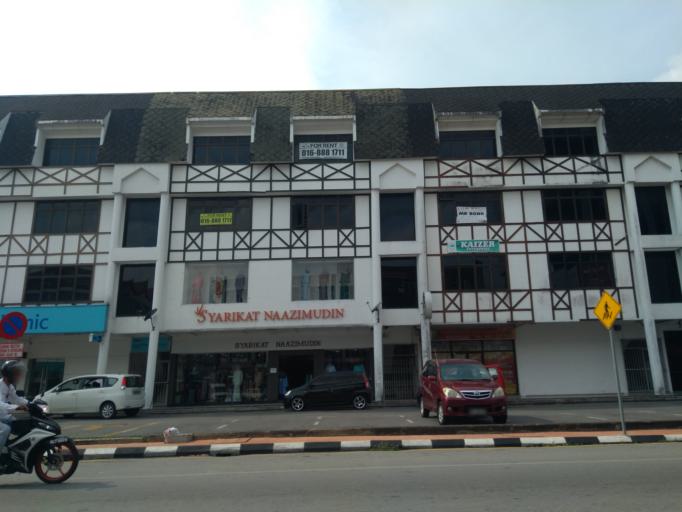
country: MY
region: Sarawak
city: Kuching
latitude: 1.5541
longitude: 110.3345
